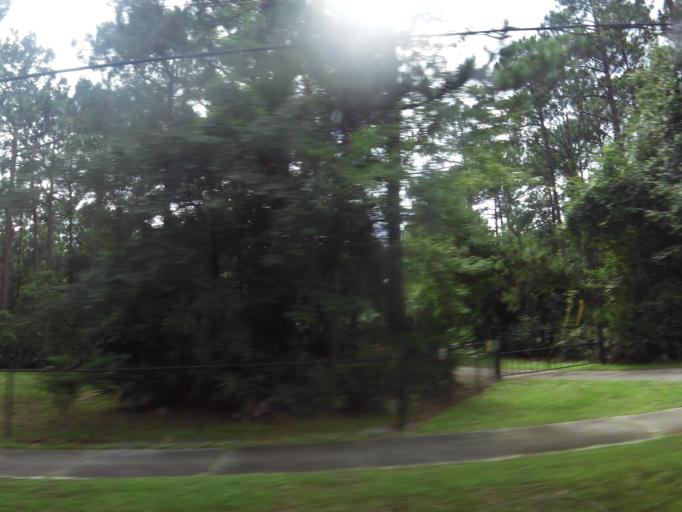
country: US
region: Florida
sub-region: Duval County
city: Jacksonville
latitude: 30.3010
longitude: -81.5306
